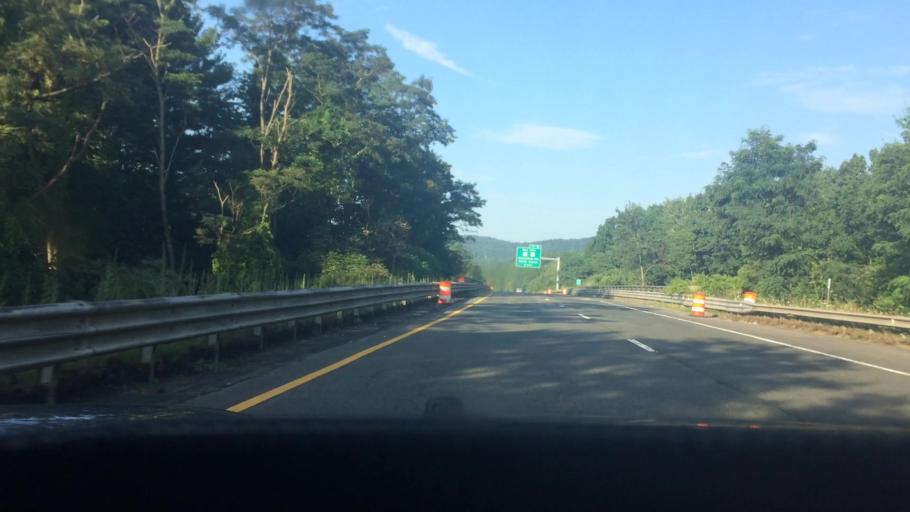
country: US
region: Massachusetts
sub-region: Franklin County
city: Greenfield
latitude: 42.6131
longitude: -72.6017
